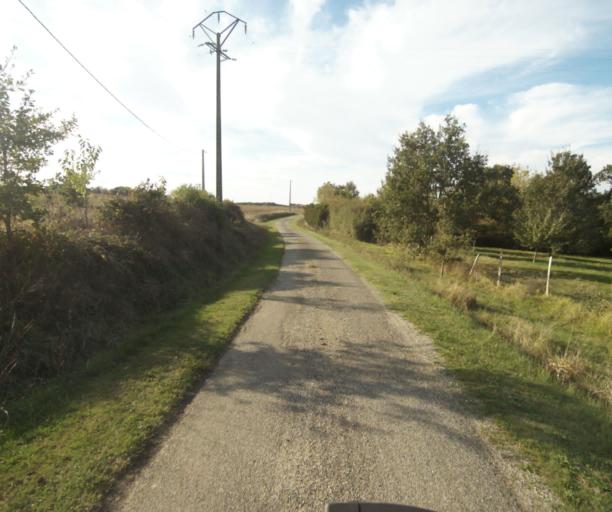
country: FR
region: Midi-Pyrenees
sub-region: Departement du Tarn-et-Garonne
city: Finhan
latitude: 43.9117
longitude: 1.1078
